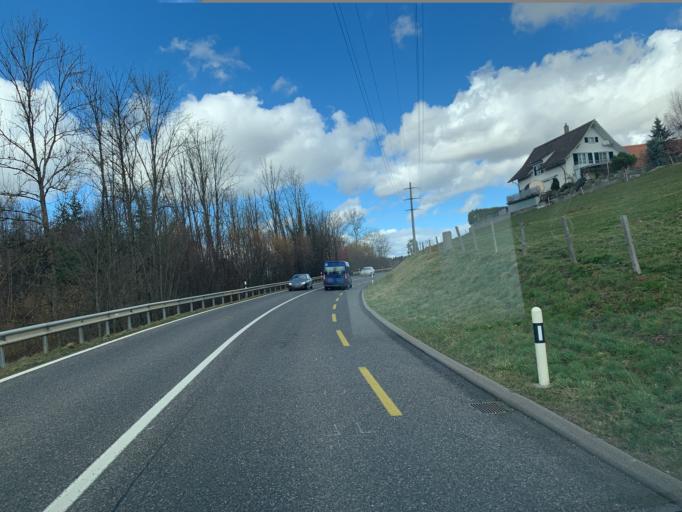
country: CH
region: Fribourg
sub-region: Sense District
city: Dudingen
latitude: 46.8731
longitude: 7.1913
